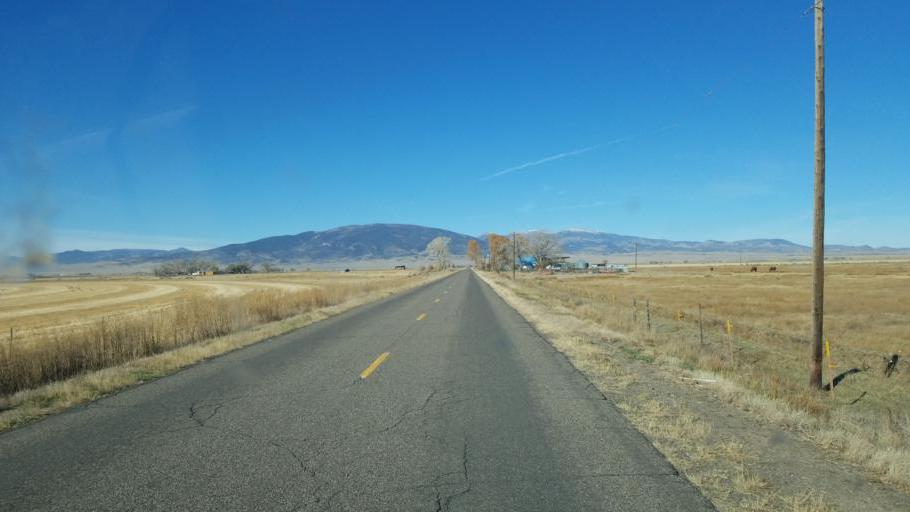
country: US
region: Colorado
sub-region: Rio Grande County
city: Monte Vista
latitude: 37.4591
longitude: -106.0804
